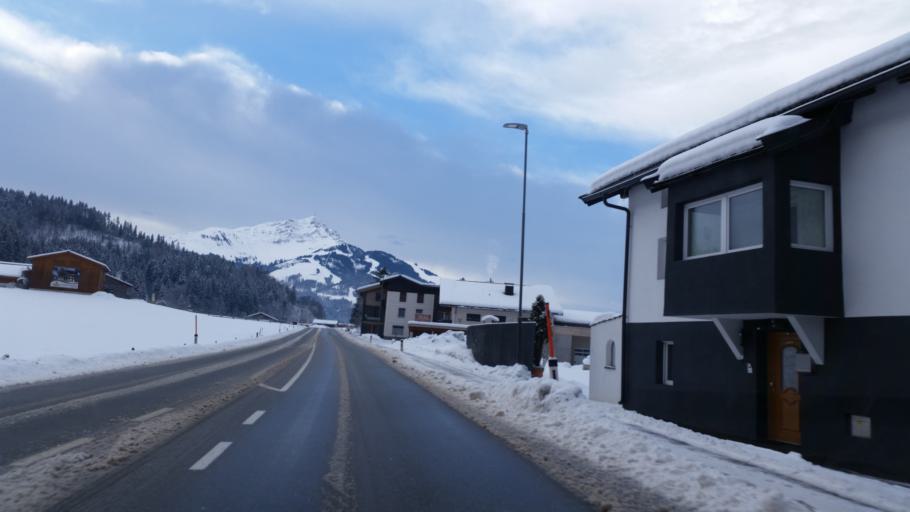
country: AT
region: Tyrol
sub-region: Politischer Bezirk Kitzbuhel
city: Kirchdorf in Tirol
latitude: 47.5510
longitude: 12.4512
